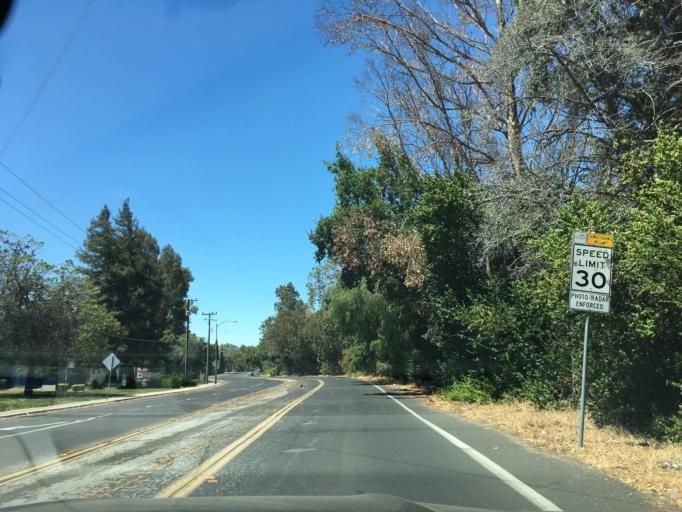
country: US
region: California
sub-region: Santa Clara County
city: East Foothills
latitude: 37.3914
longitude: -121.8387
